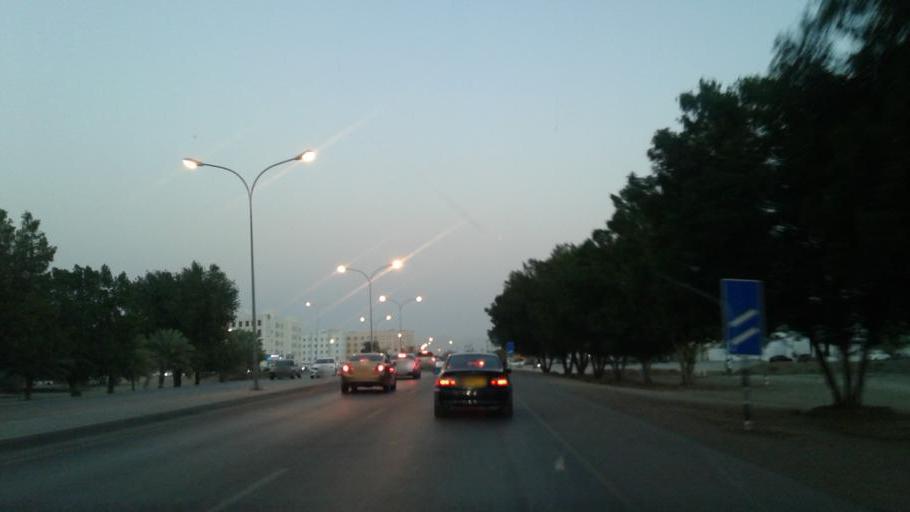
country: OM
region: Muhafazat Masqat
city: As Sib al Jadidah
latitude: 23.6112
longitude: 58.2395
